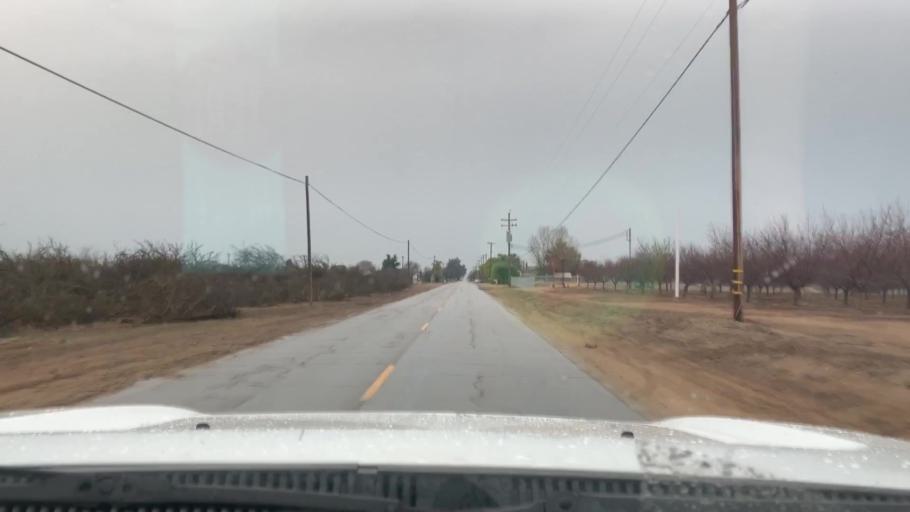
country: US
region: California
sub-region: Kern County
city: Shafter
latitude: 35.4781
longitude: -119.2708
